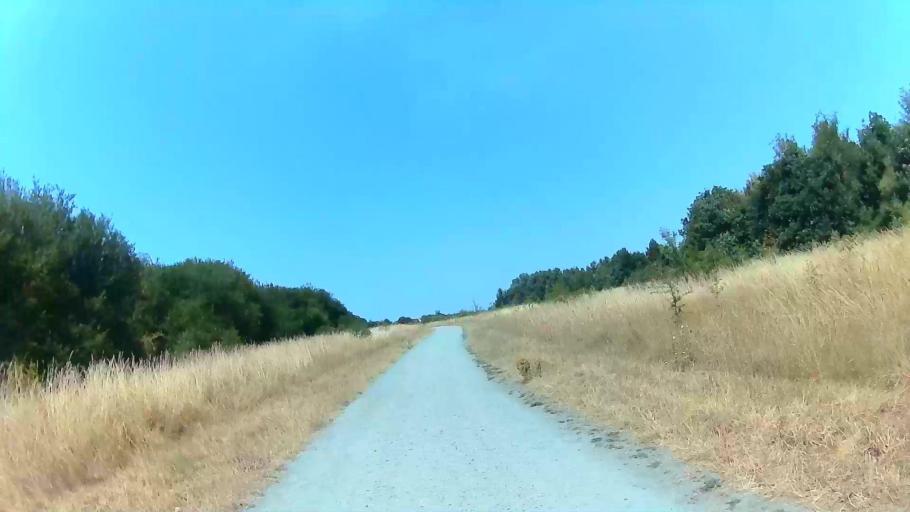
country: GB
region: England
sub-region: Greater London
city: Elm Park
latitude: 51.5287
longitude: 0.1940
